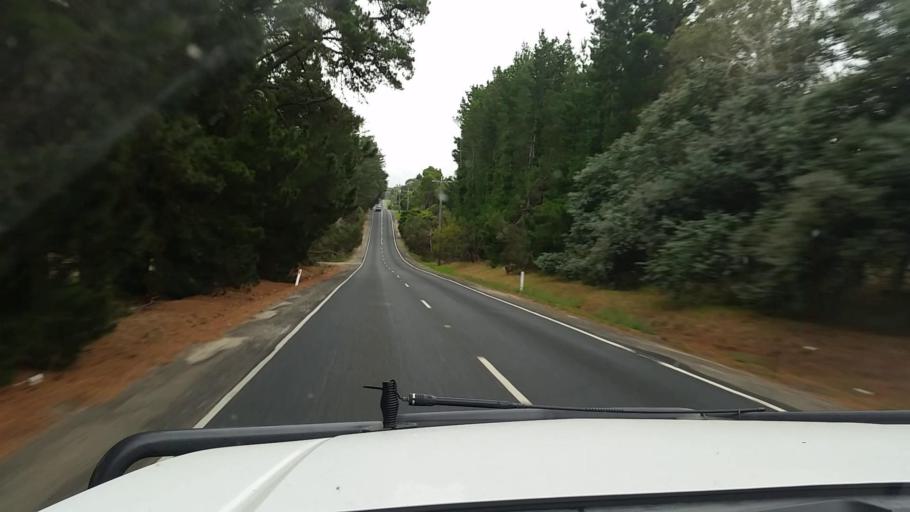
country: AU
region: Victoria
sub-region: Mornington Peninsula
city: Hastings
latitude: -38.2968
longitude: 145.1457
